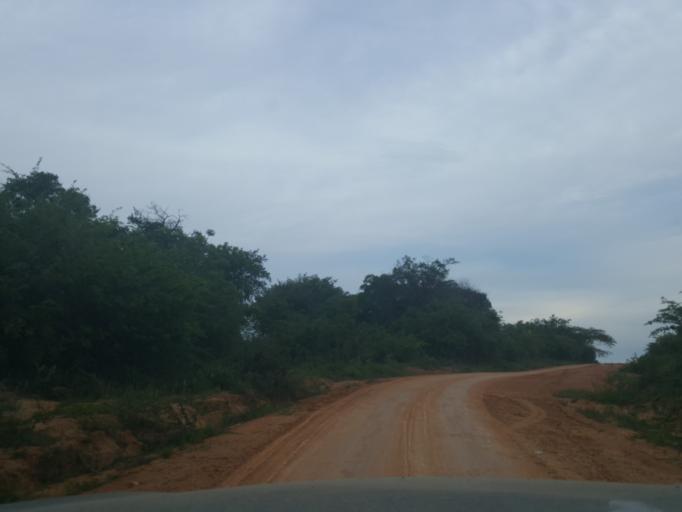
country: ZA
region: Limpopo
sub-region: Mopani District Municipality
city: Hoedspruit
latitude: -24.5910
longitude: 30.9446
